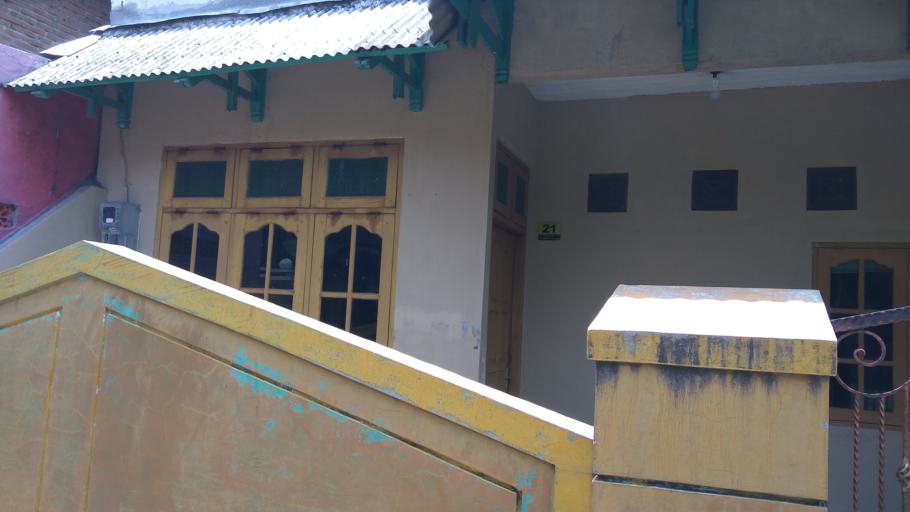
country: ID
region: Central Java
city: Grogol
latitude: -7.5900
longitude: 110.7970
